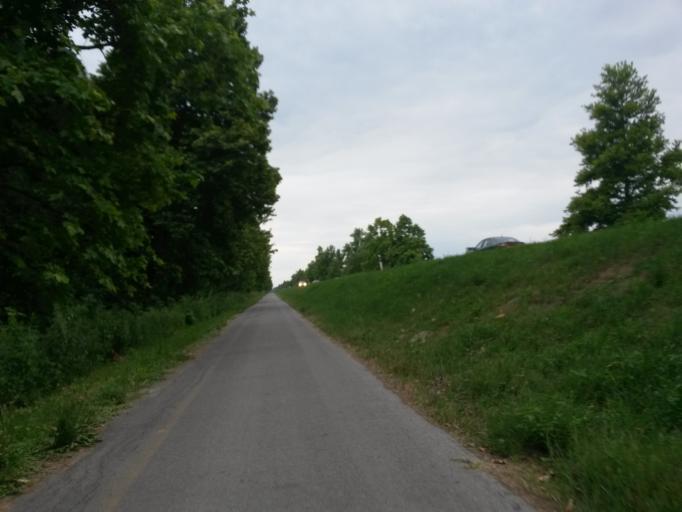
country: HR
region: Osjecko-Baranjska
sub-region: Grad Osijek
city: Bilje
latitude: 45.5883
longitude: 18.7330
